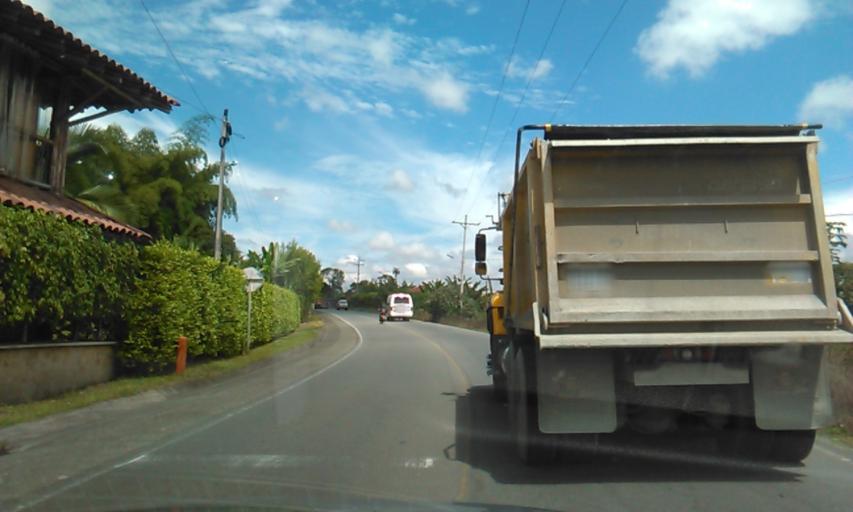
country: CO
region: Quindio
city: Cordoba
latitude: 4.4345
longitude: -75.7172
